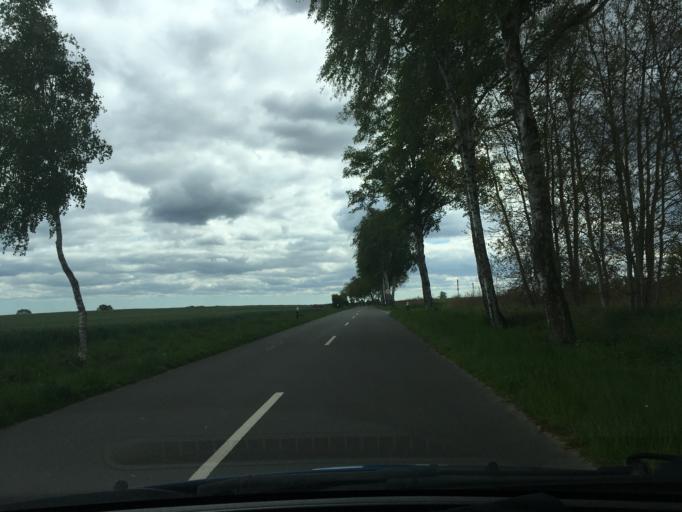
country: DE
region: Lower Saxony
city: Suderburg
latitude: 52.8720
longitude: 10.4092
